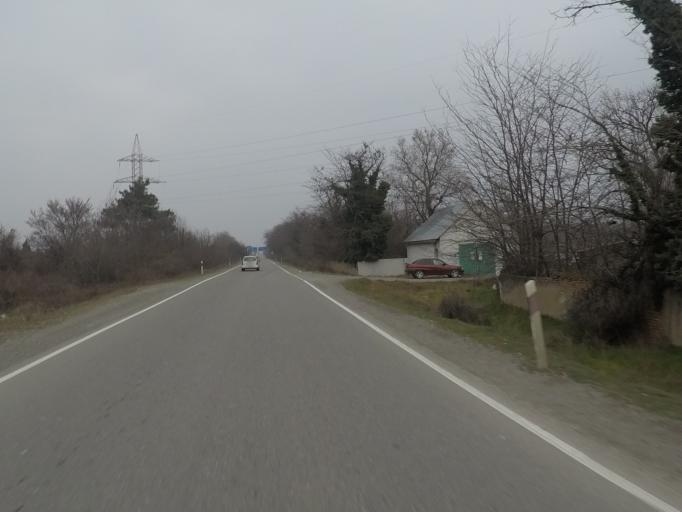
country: GE
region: Mtskheta-Mtianeti
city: Mtskheta
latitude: 41.8915
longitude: 44.7176
